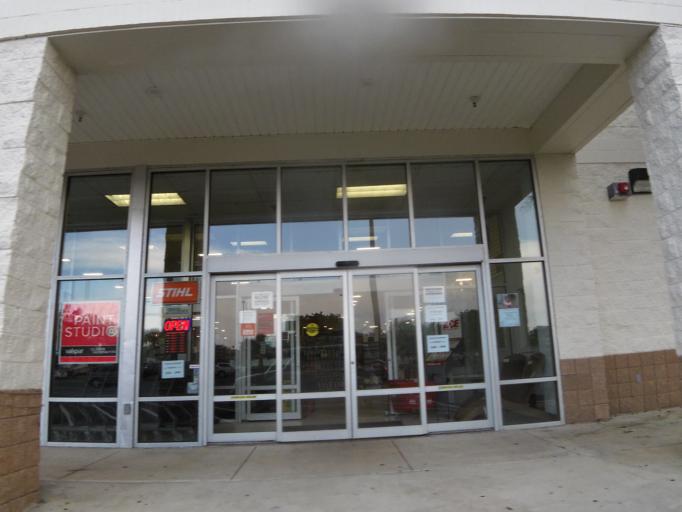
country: US
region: Florida
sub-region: Saint Johns County
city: Ponte Vedra Beach
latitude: 30.2540
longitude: -81.3935
